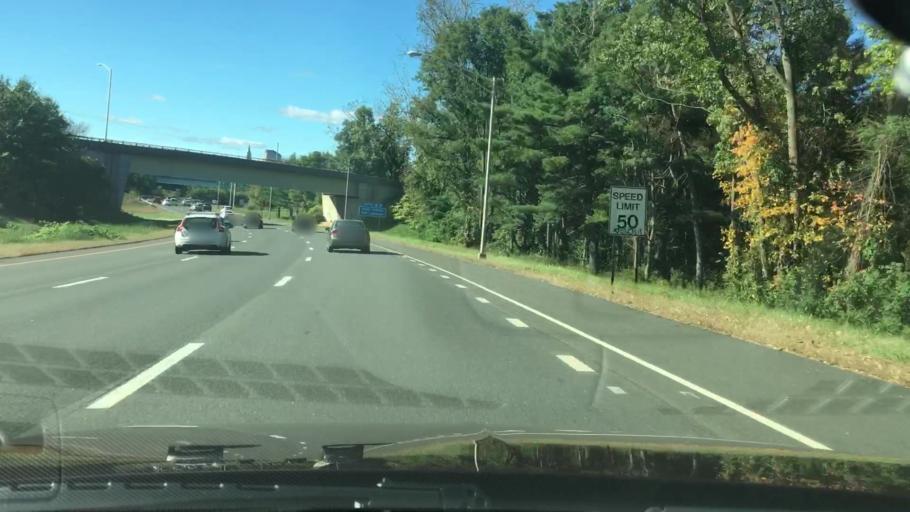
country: US
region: Connecticut
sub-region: Hartford County
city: Wethersfield
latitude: 41.7537
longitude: -72.6456
